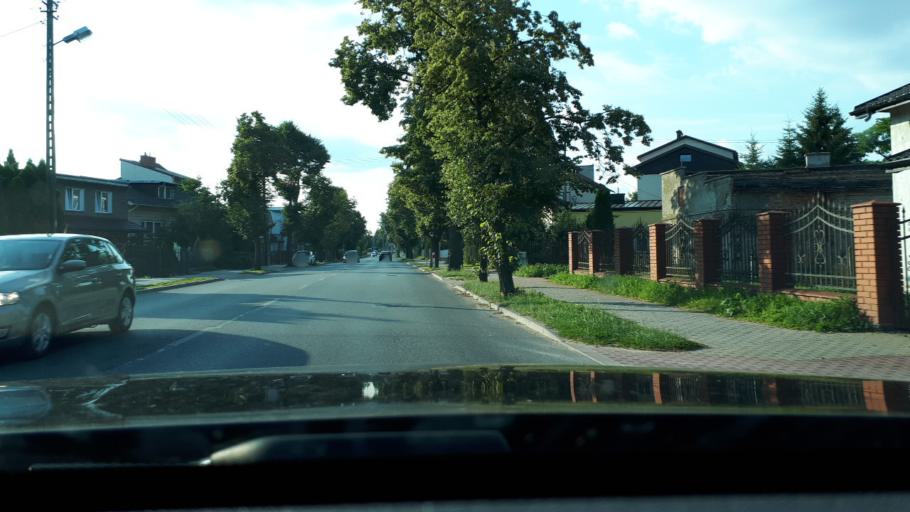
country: PL
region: Masovian Voivodeship
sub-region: Powiat ciechanowski
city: Ciechanow
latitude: 52.8648
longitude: 20.6275
